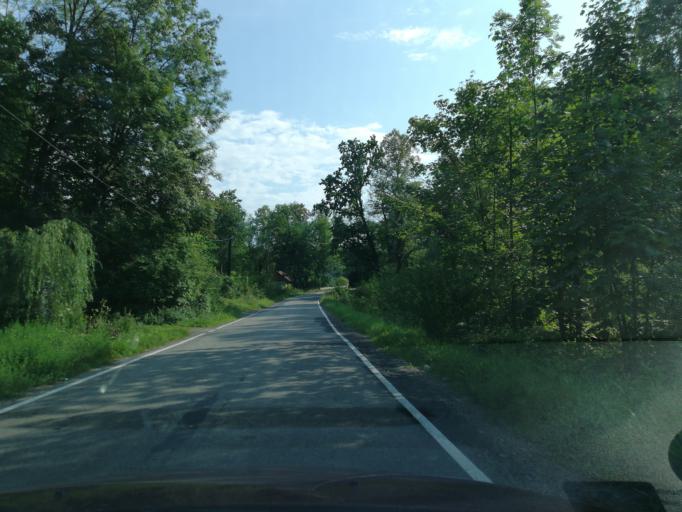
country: PL
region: Lesser Poland Voivodeship
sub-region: Powiat nowosadecki
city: Nawojowa
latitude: 49.5535
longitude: 20.7453
